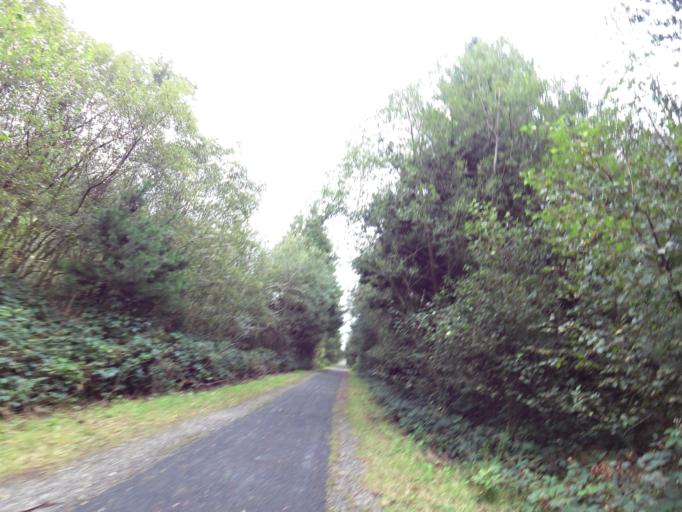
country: IE
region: Leinster
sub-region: Uibh Fhaili
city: Ferbane
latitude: 53.2147
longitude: -7.7511
